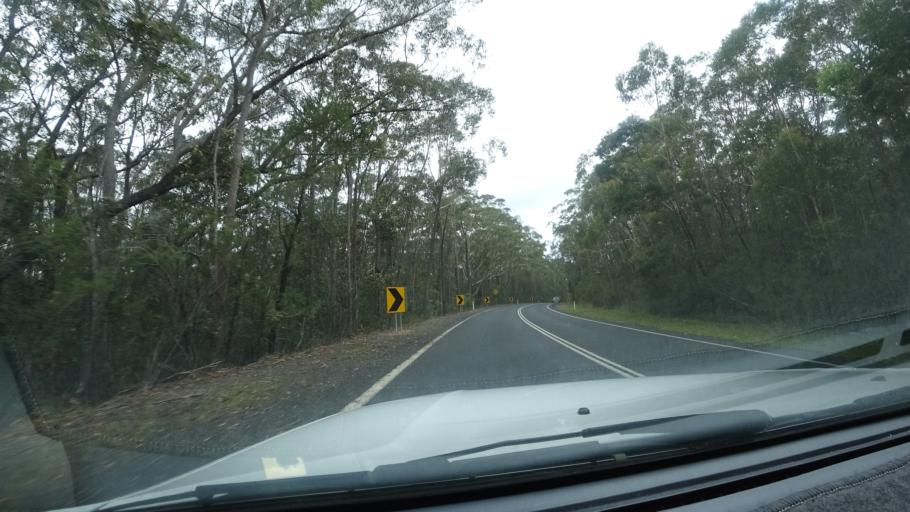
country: AU
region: New South Wales
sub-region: Shoalhaven Shire
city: Milton
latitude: -35.1945
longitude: 150.4420
